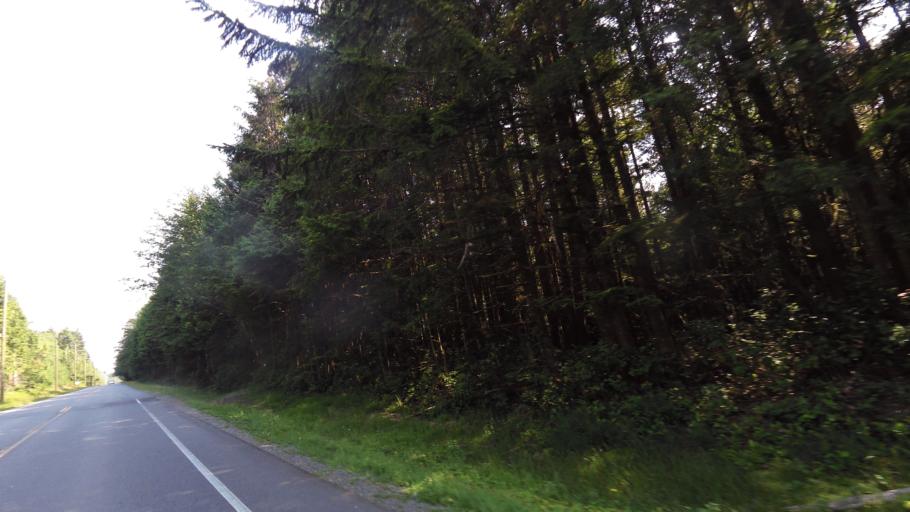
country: CA
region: British Columbia
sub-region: Regional District of Alberni-Clayoquot
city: Ucluelet
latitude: 49.0512
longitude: -125.7097
